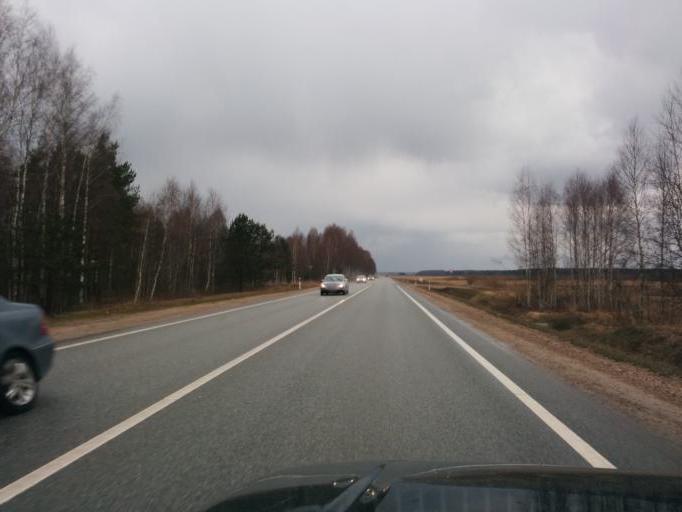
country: LV
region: Marupe
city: Marupe
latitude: 56.8482
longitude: 24.0115
